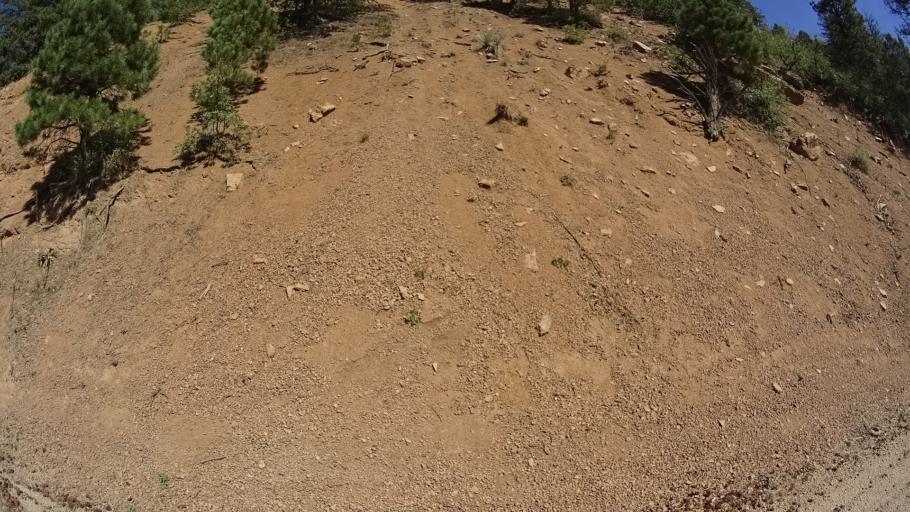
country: US
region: Colorado
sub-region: El Paso County
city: Colorado Springs
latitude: 38.7955
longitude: -104.8791
